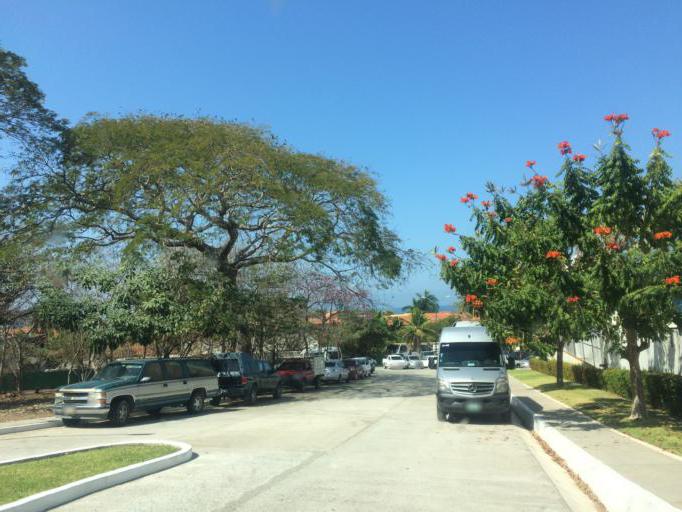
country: MX
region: Guerrero
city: Ixtapa
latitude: 17.6741
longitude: -101.6409
